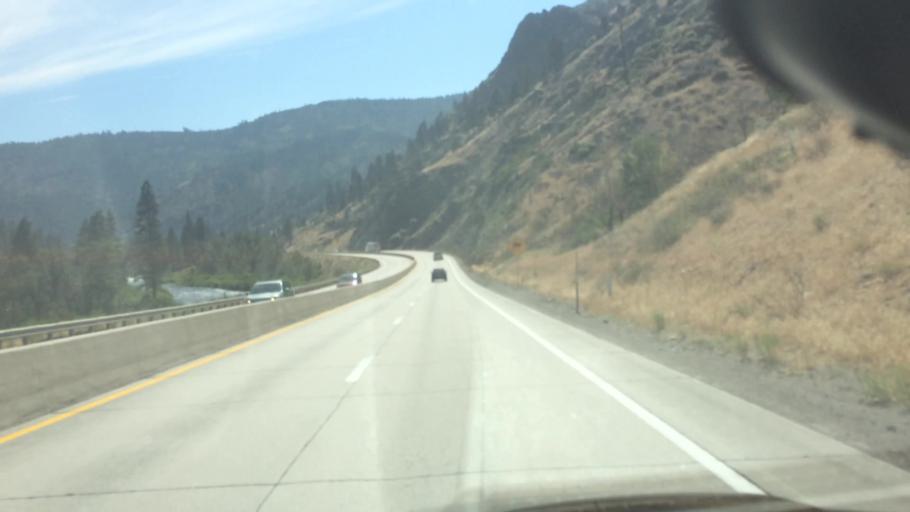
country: US
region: Nevada
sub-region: Washoe County
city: Verdi
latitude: 39.4417
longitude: -120.0149
